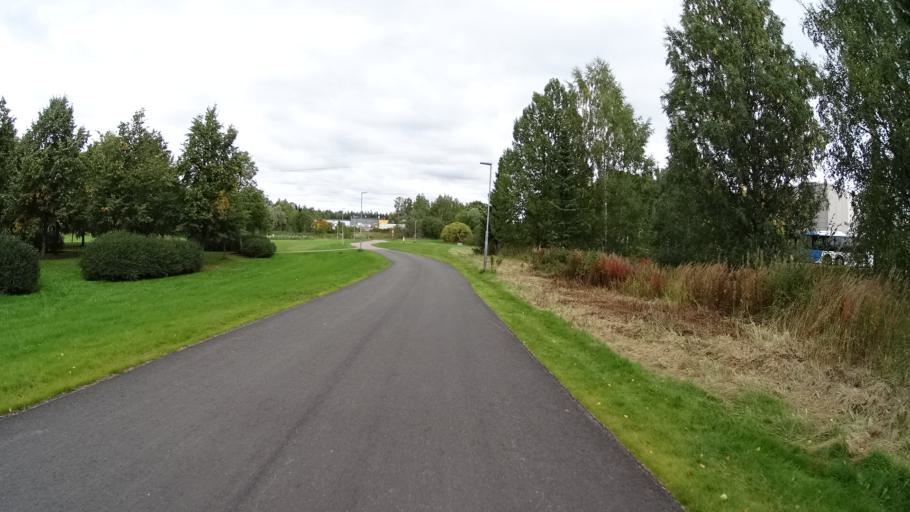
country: FI
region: Uusimaa
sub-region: Helsinki
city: Helsinki
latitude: 60.2382
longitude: 24.9758
